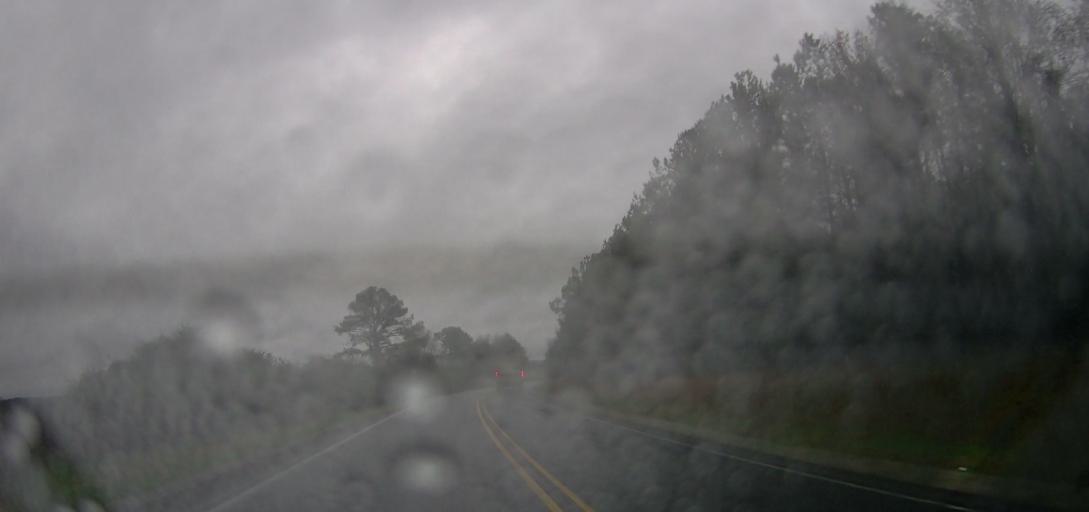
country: US
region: Alabama
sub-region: Chilton County
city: Clanton
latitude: 32.6272
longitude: -86.7380
